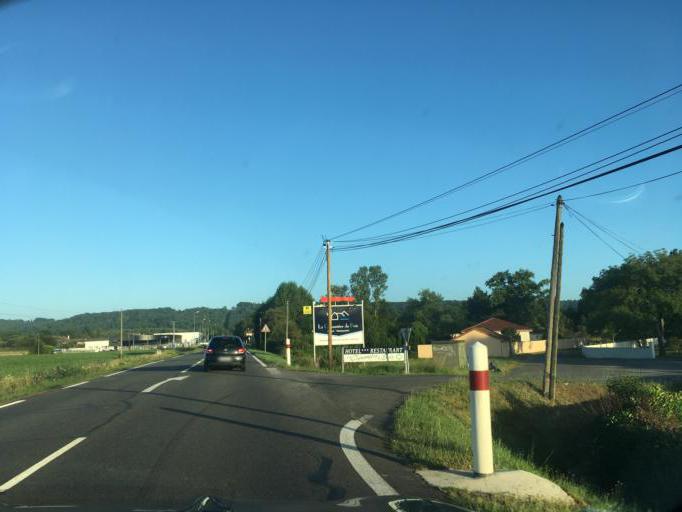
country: FR
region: Midi-Pyrenees
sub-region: Departement des Hautes-Pyrenees
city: Ibos
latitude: 43.2424
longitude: -0.0008
